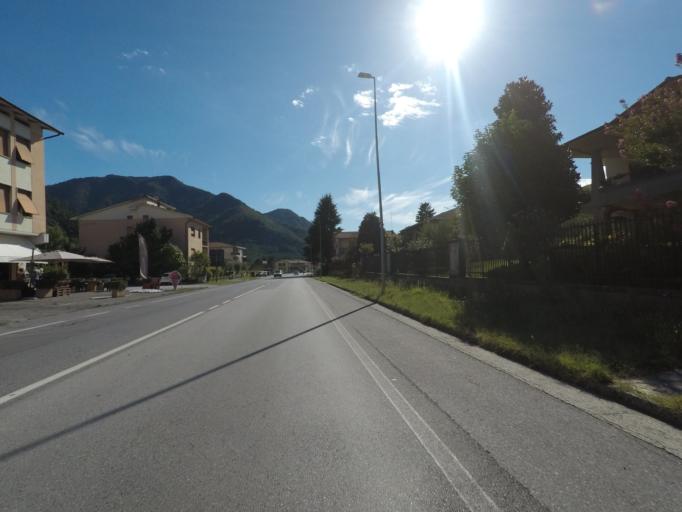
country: IT
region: Tuscany
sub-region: Provincia di Lucca
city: Borgo a Mozzano
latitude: 43.9791
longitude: 10.5491
